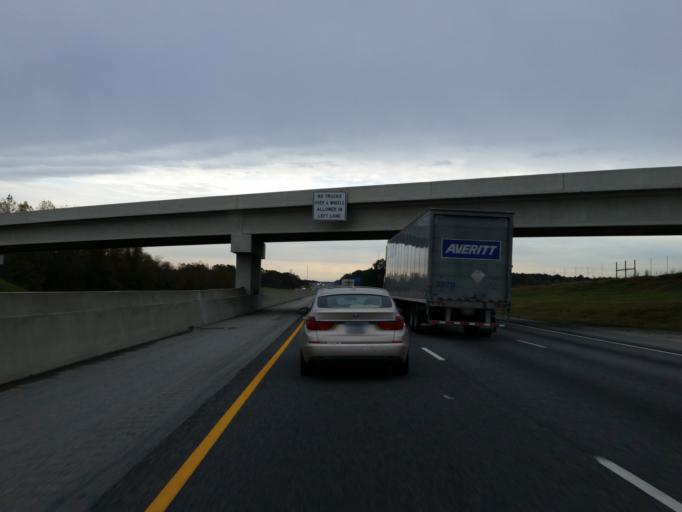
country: US
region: Georgia
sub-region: Turner County
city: Ashburn
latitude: 31.6465
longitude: -83.5924
